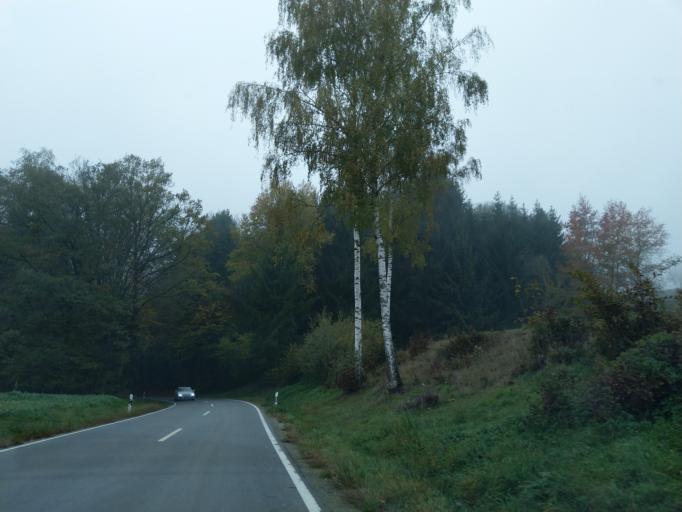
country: DE
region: Bavaria
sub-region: Lower Bavaria
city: Grattersdorf
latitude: 48.7916
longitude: 13.1506
